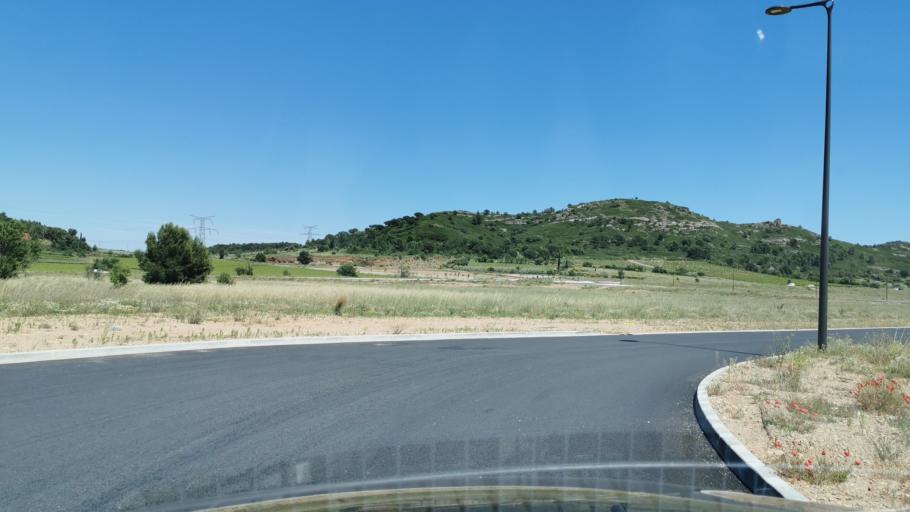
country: FR
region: Languedoc-Roussillon
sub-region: Departement de l'Aude
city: Nevian
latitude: 43.1974
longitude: 2.8949
